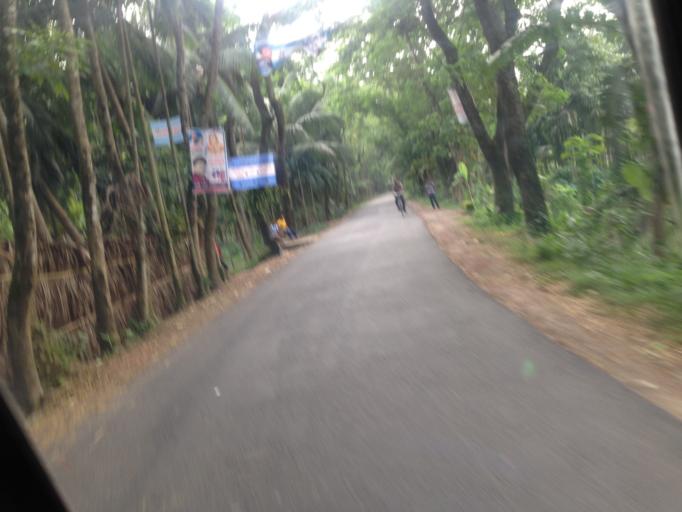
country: BD
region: Chittagong
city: Raipur
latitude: 23.0362
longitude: 90.7425
